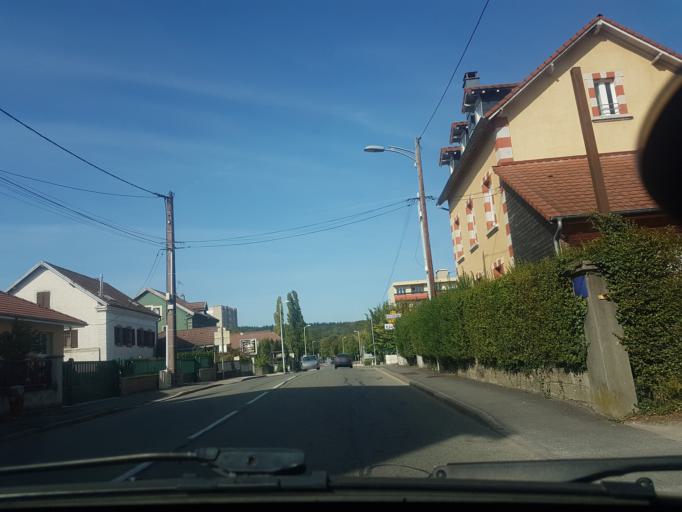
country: FR
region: Franche-Comte
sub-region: Territoire de Belfort
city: Offemont
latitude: 47.6542
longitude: 6.8626
